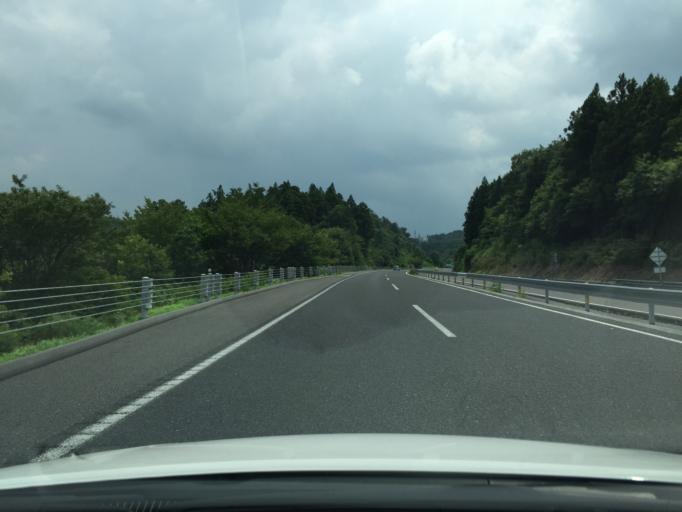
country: JP
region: Fukushima
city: Funehikimachi-funehiki
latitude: 37.3041
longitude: 140.6134
